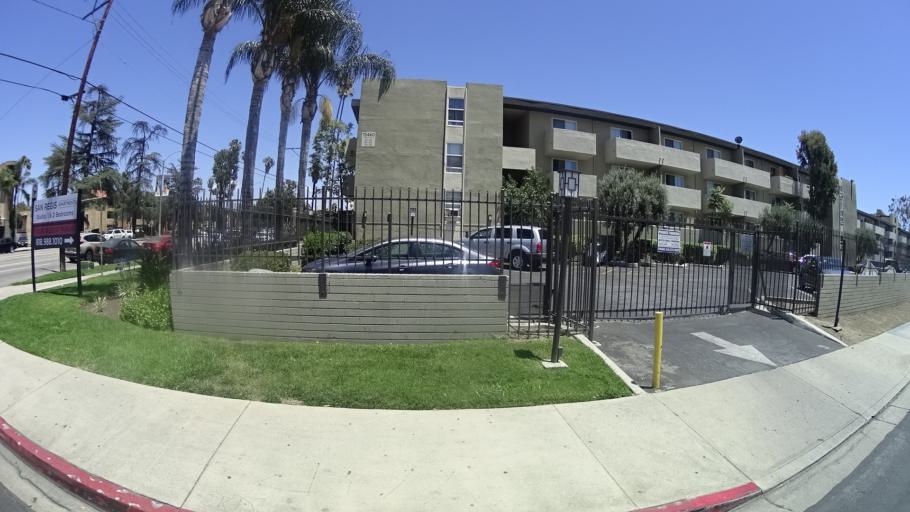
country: US
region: California
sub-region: Los Angeles County
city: Van Nuys
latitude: 34.2010
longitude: -118.4706
